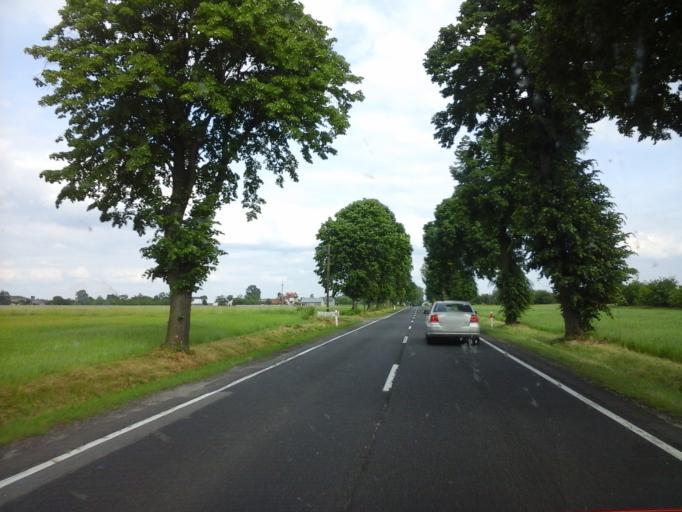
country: PL
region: Lodz Voivodeship
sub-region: Powiat opoczynski
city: Mniszkow
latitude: 51.3322
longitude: 20.0225
